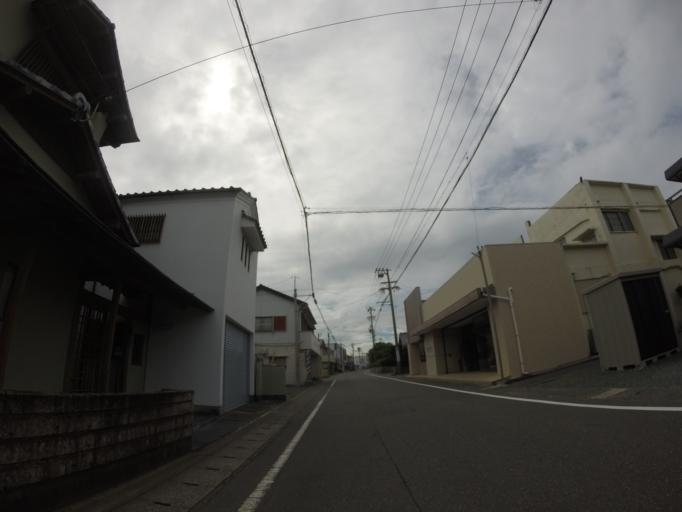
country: JP
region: Shizuoka
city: Oyama
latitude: 34.6033
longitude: 138.2171
